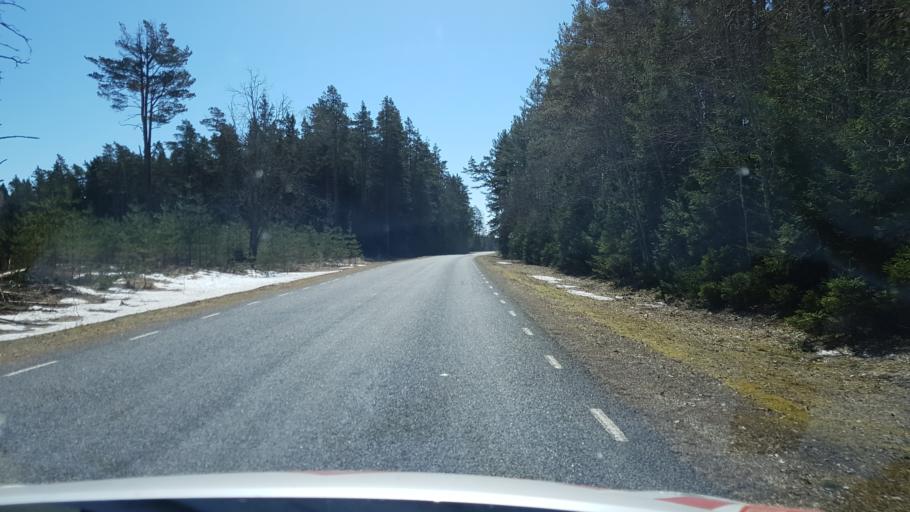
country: EE
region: Laeaene-Virumaa
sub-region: Haljala vald
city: Haljala
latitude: 59.4969
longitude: 26.2421
